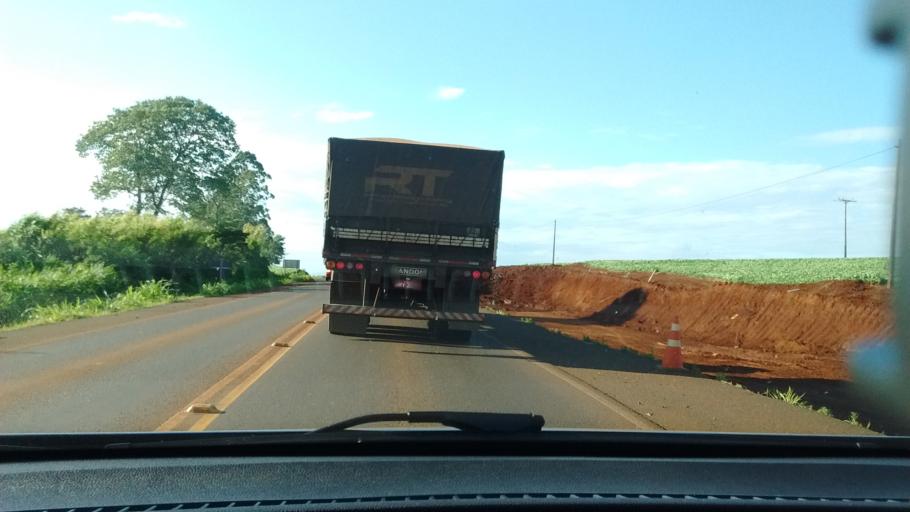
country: BR
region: Parana
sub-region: Cascavel
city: Cascavel
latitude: -25.2194
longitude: -53.5954
